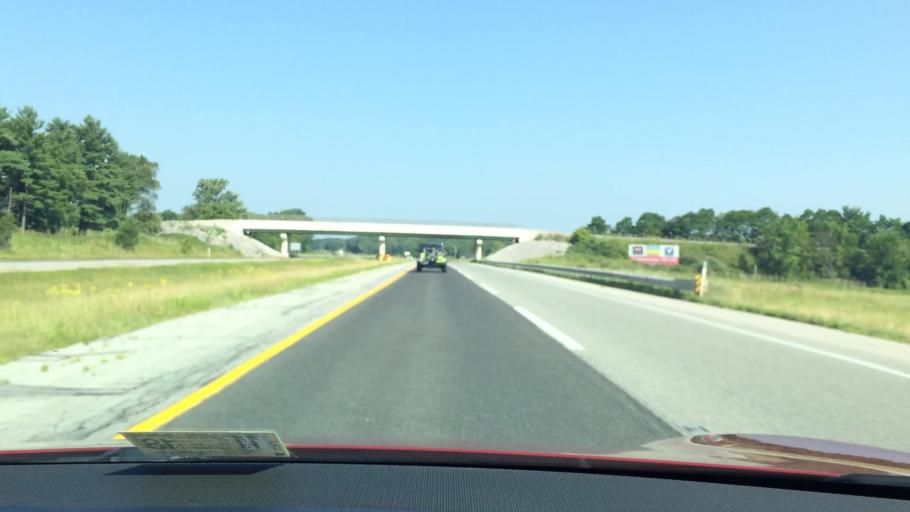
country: US
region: Indiana
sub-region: Steuben County
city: Fremont
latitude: 41.6998
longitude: -84.9163
